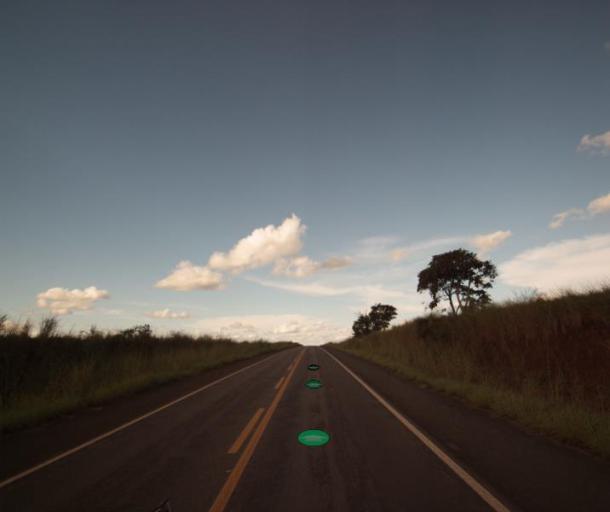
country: BR
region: Goias
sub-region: Itaberai
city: Itaberai
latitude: -15.9679
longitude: -49.6682
